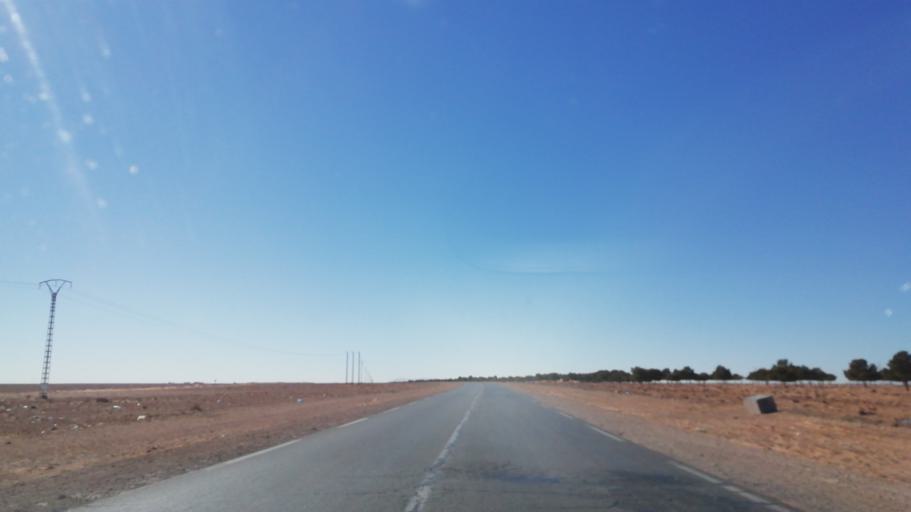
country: DZ
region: Saida
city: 'Ain el Hadjar
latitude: 34.0032
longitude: 0.0456
